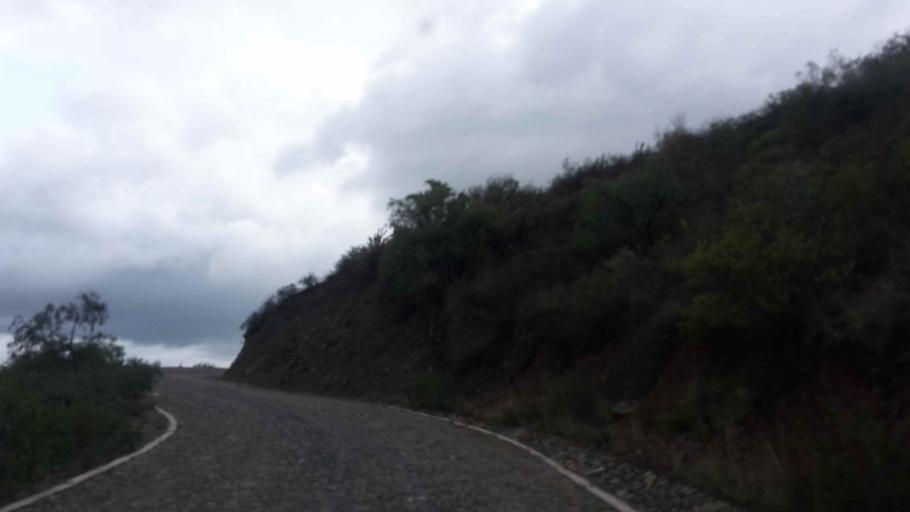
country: BO
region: Cochabamba
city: Cochabamba
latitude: -17.3674
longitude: -66.0617
